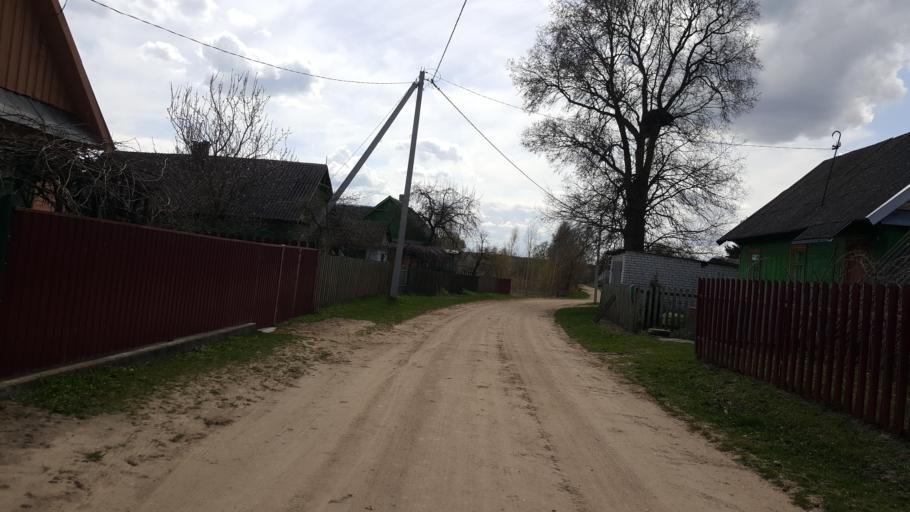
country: BY
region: Brest
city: Kamyanyets
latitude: 52.3537
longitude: 23.7331
